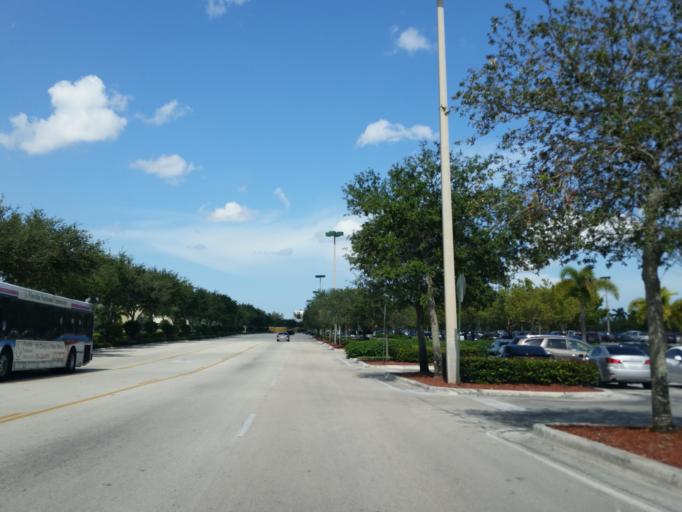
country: US
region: Florida
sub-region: Miami-Dade County
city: Sweetwater
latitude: 25.7903
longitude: -80.3817
